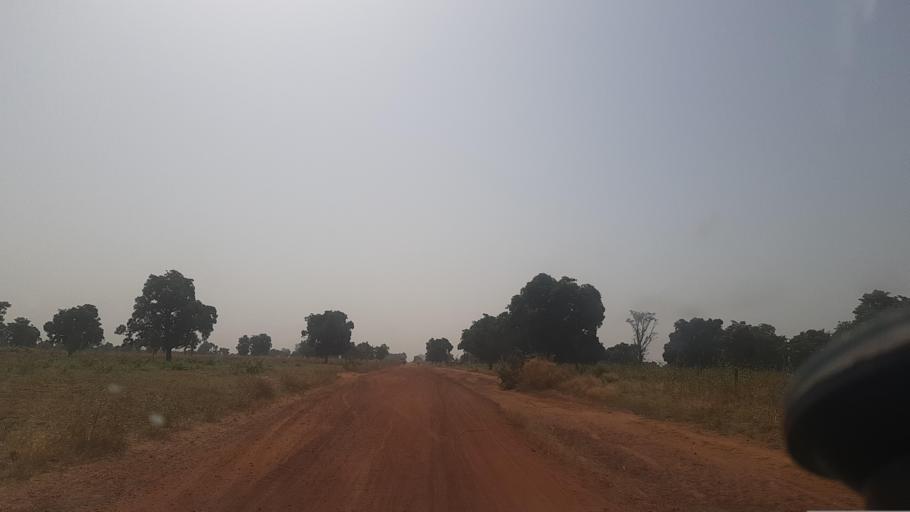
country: ML
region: Segou
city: Baroueli
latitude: 13.0038
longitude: -6.4197
